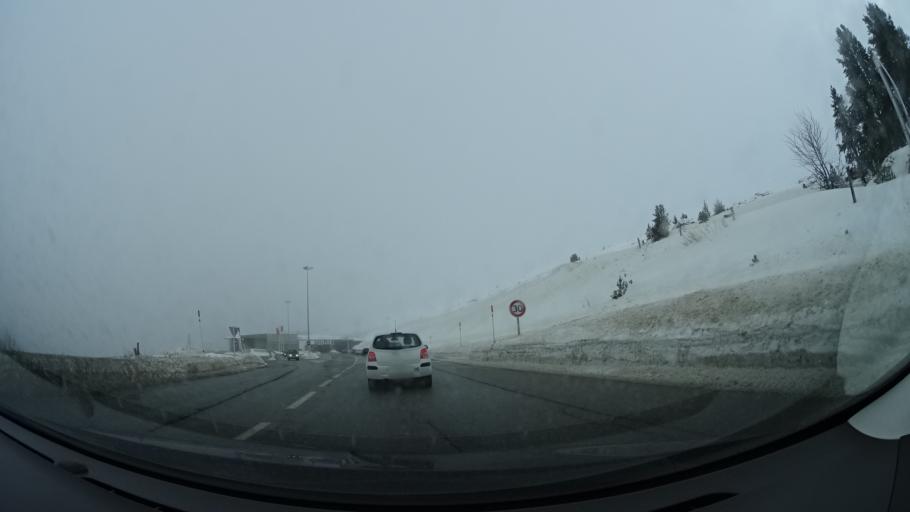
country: AD
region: Encamp
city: Pas de la Casa
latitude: 42.5589
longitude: 1.7539
